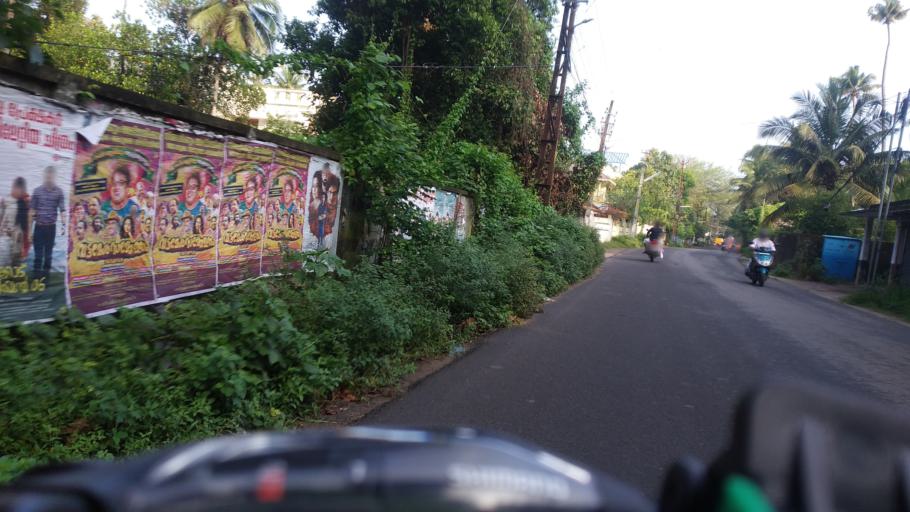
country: IN
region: Kerala
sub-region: Ernakulam
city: Elur
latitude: 10.0690
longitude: 76.2123
